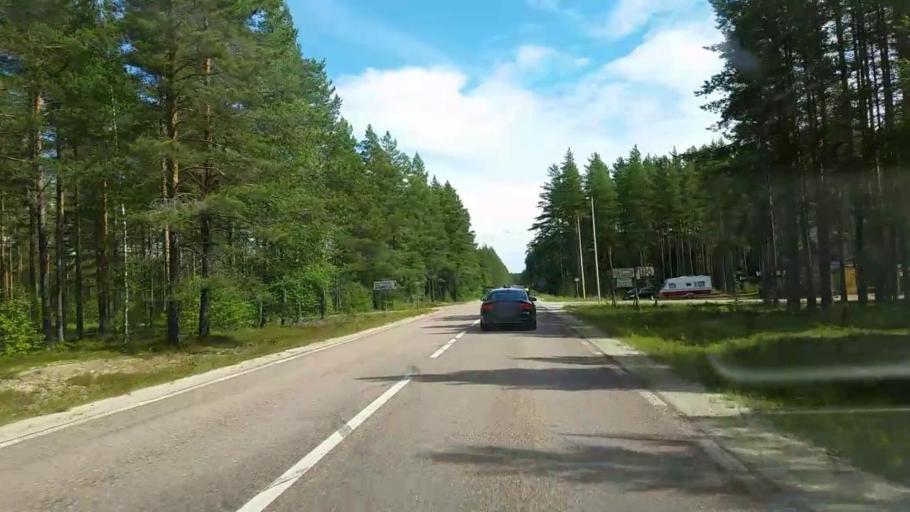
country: SE
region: Dalarna
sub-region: Rattviks Kommun
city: Raettvik
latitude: 61.1736
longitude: 15.1650
